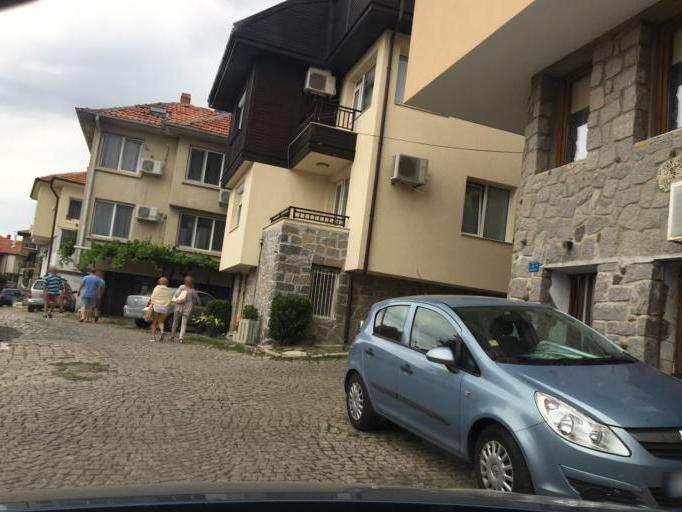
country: BG
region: Burgas
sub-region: Obshtina Sozopol
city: Sozopol
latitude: 42.4251
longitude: 27.6957
